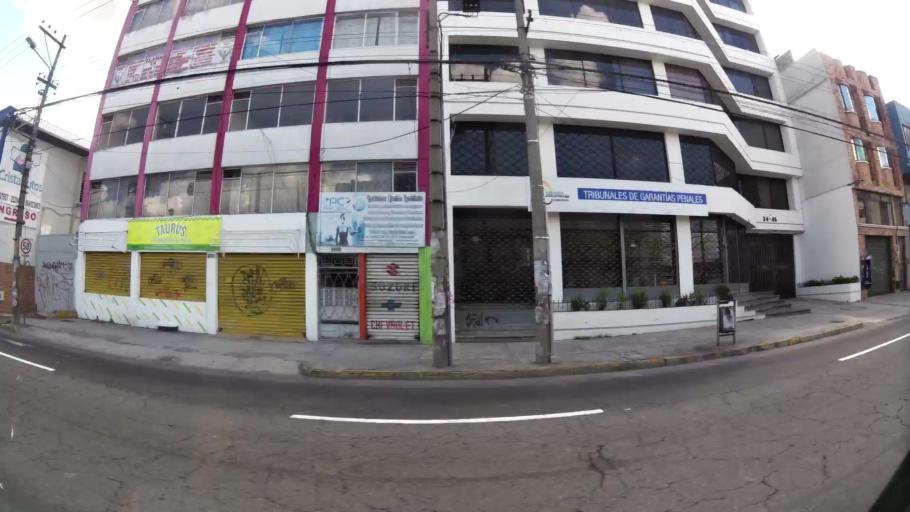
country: EC
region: Pichincha
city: Quito
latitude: -0.1906
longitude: -78.4930
